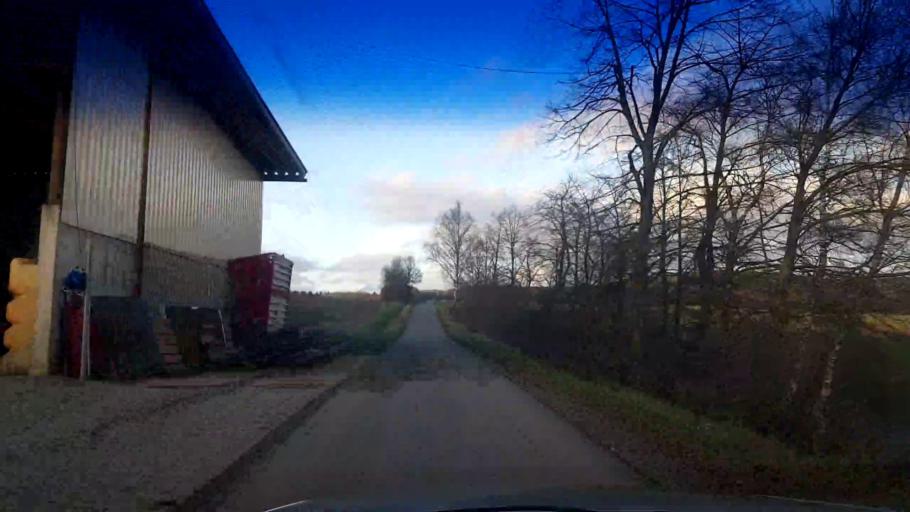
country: DE
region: Bavaria
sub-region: Upper Franconia
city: Buttenheim
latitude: 49.8098
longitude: 11.0394
